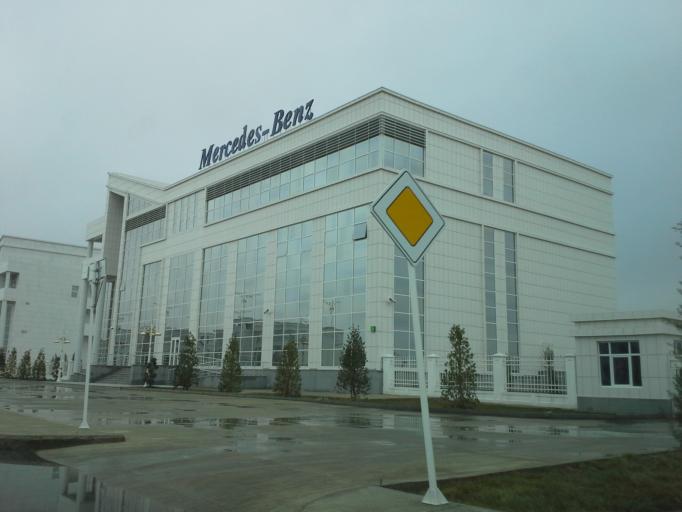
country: TM
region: Ahal
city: Ashgabat
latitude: 37.9662
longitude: 58.4107
